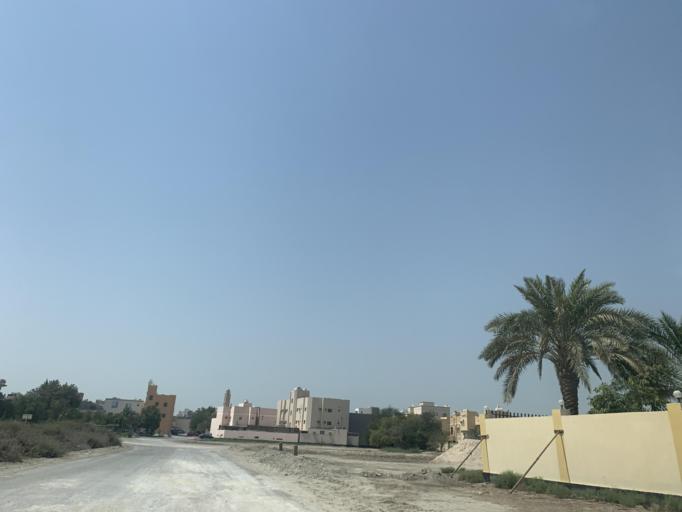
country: BH
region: Manama
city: Jidd Hafs
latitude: 26.2005
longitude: 50.5209
